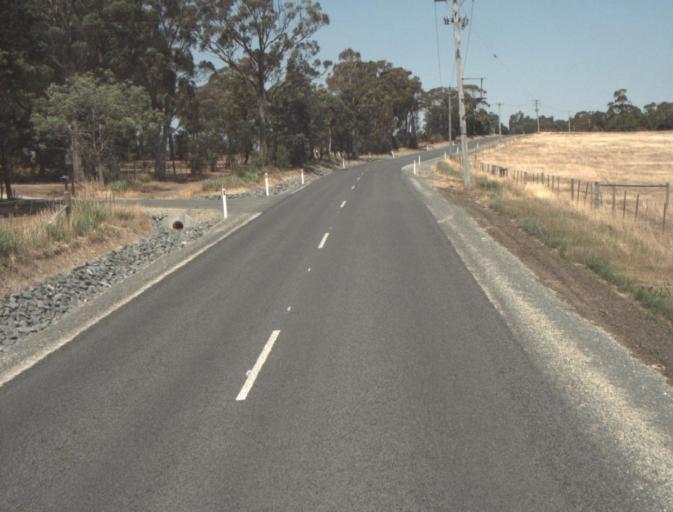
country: AU
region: Tasmania
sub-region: Launceston
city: Newstead
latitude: -41.4827
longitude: 147.1921
